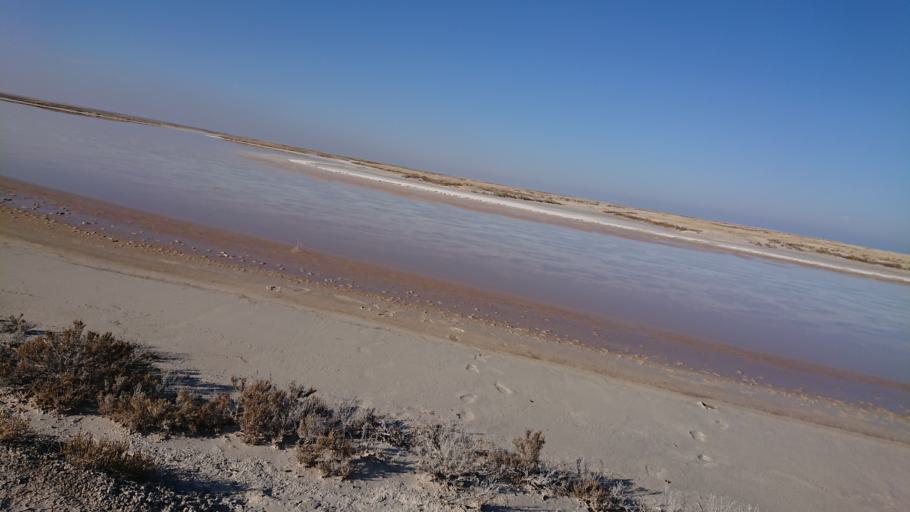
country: TR
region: Aksaray
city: Eskil
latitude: 38.4294
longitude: 33.5071
